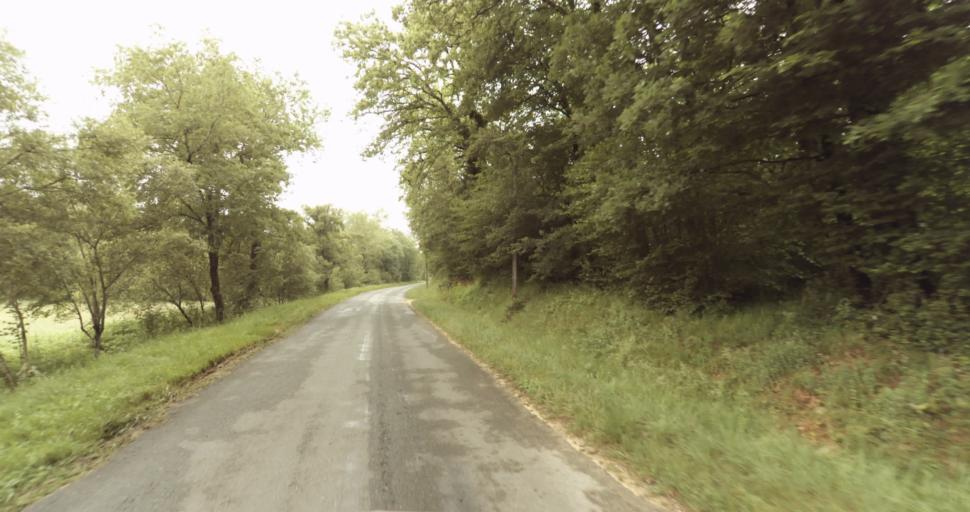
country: FR
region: Aquitaine
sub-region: Departement de la Dordogne
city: Lalinde
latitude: 44.8860
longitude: 0.7740
